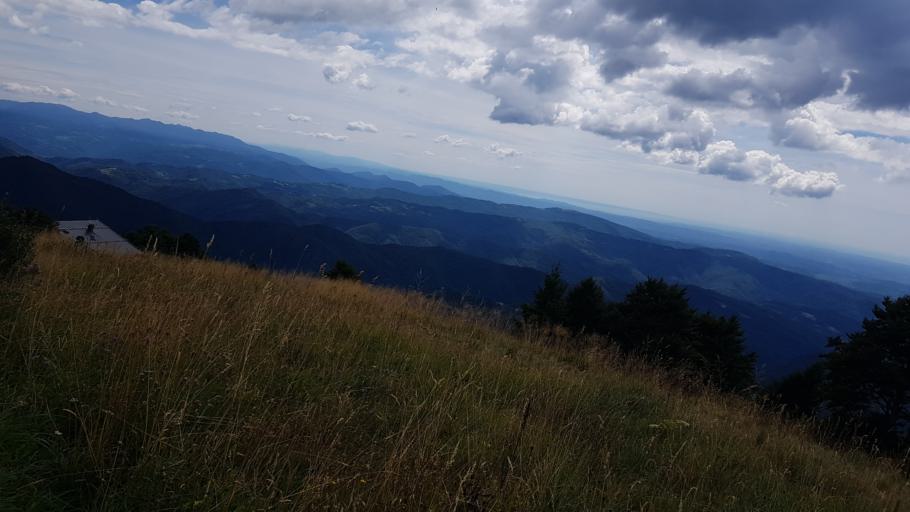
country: IT
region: Friuli Venezia Giulia
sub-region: Provincia di Udine
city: Savogna
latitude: 46.2038
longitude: 13.5373
